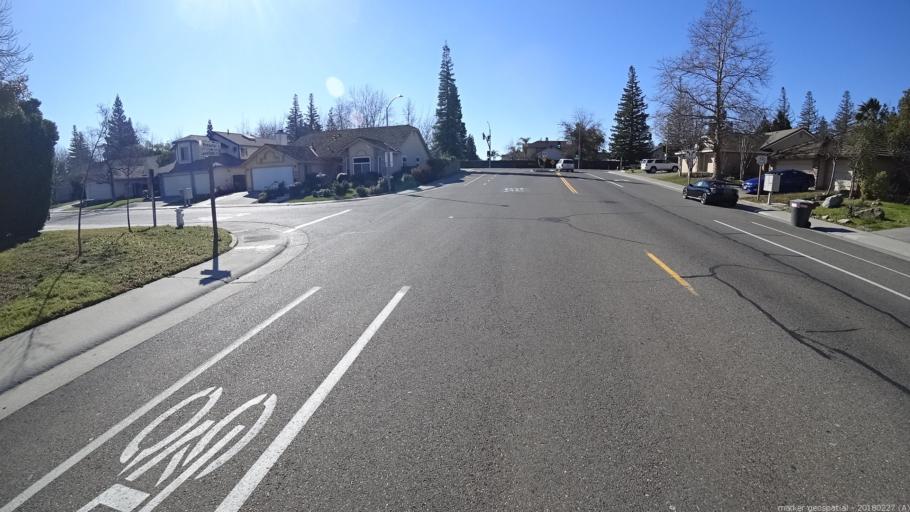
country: US
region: California
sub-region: Sacramento County
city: North Highlands
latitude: 38.7222
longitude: -121.3689
